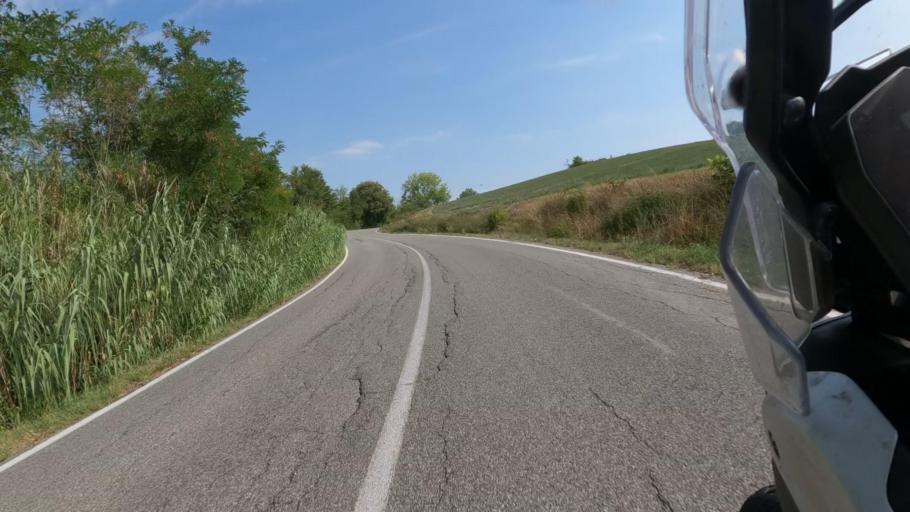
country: IT
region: Piedmont
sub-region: Provincia di Alessandria
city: Rosignano Monferrato
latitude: 45.0785
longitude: 8.4101
